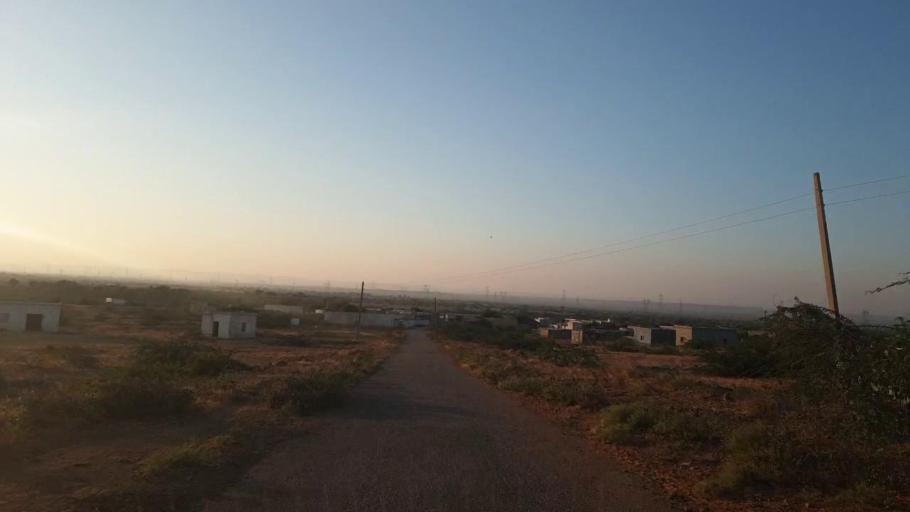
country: PK
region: Sindh
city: Gharo
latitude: 25.1663
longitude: 67.6692
